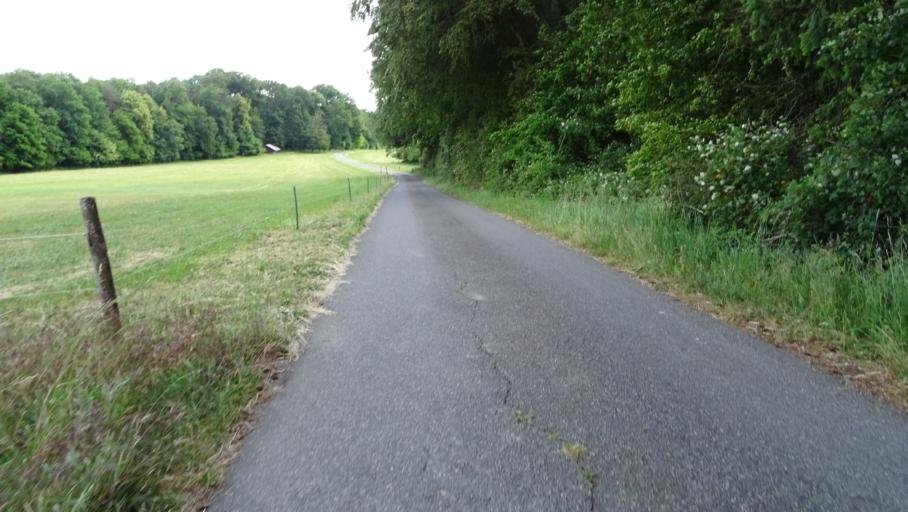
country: DE
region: Baden-Wuerttemberg
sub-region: Karlsruhe Region
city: Hassmersheim
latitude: 49.3130
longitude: 9.1574
